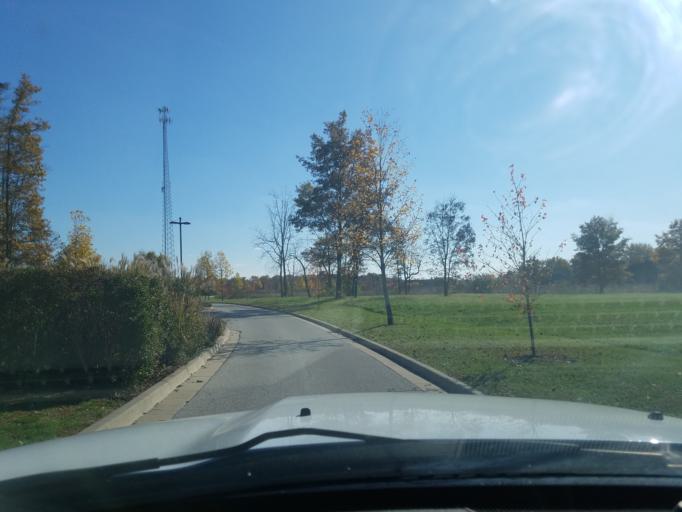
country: US
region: Indiana
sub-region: Montgomery County
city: Crawfordsville
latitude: 40.0747
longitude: -86.9038
